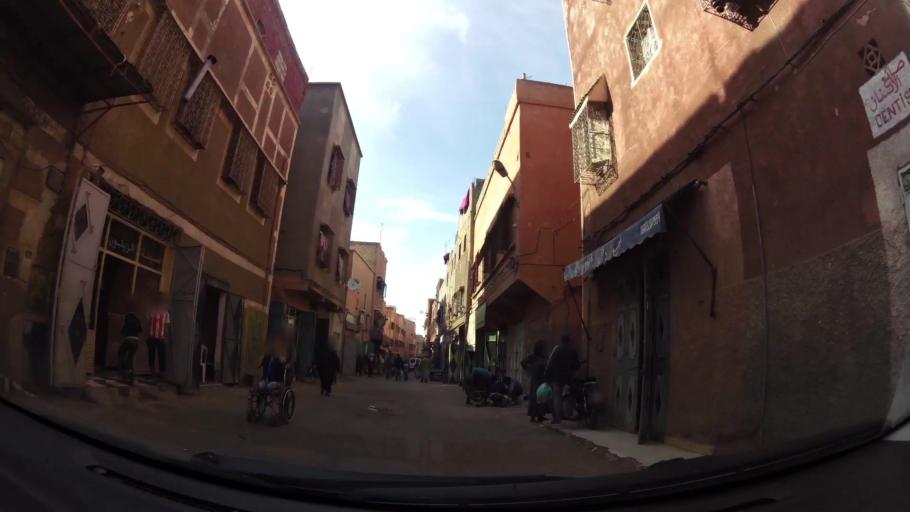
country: MA
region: Marrakech-Tensift-Al Haouz
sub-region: Marrakech
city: Marrakesh
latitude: 31.6098
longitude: -7.9629
